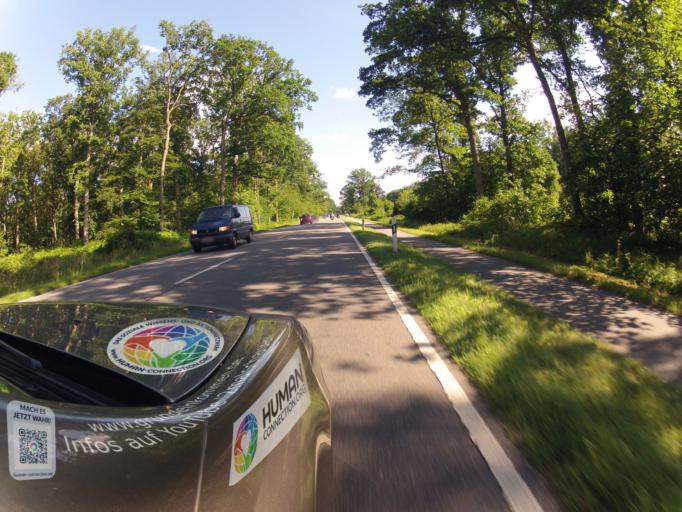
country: DE
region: Mecklenburg-Vorpommern
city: Loddin
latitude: 53.9919
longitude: 14.0715
